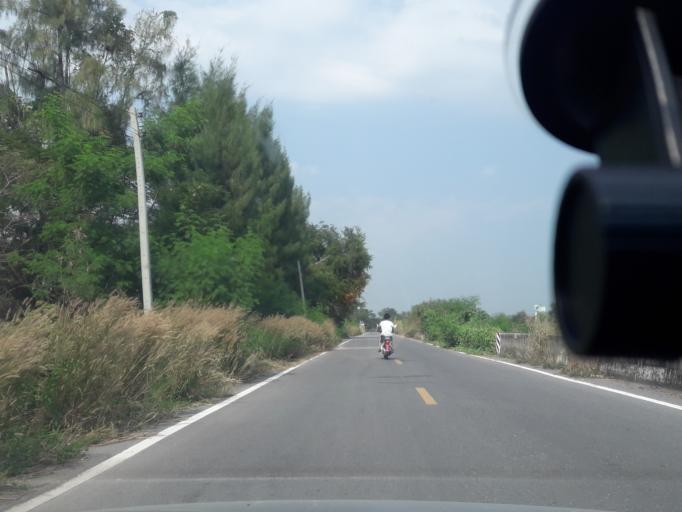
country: TH
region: Sara Buri
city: Nong Khae
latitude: 14.2719
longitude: 100.8912
